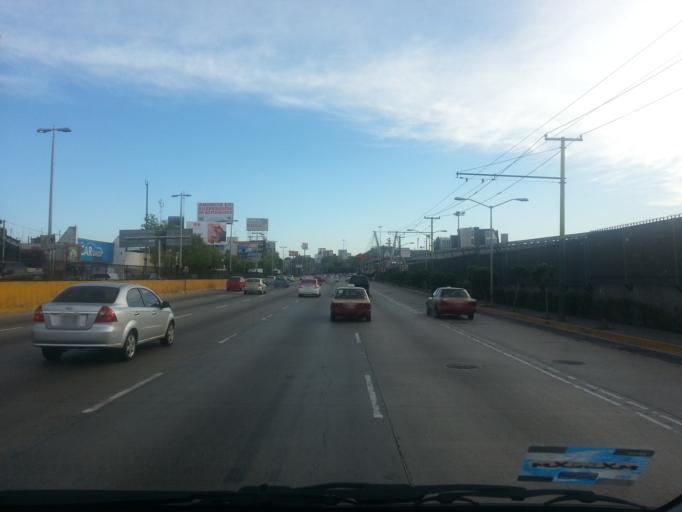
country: MX
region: Mexico City
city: Venustiano Carranza
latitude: 19.4302
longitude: -99.0905
